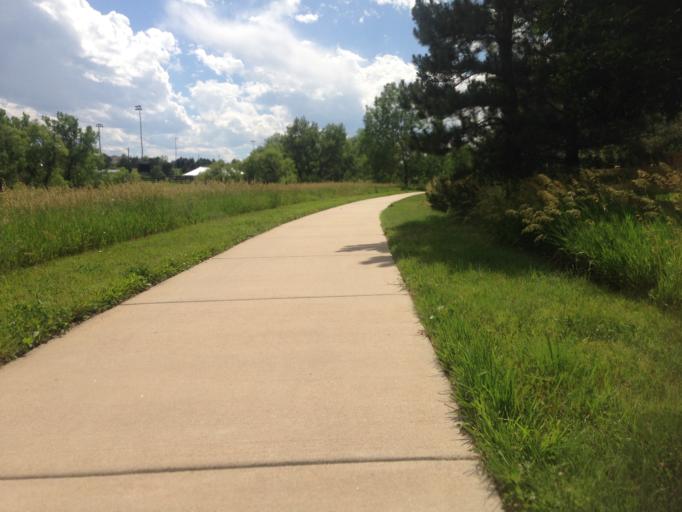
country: US
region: Colorado
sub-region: Boulder County
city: Superior
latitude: 39.9323
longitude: -105.1489
